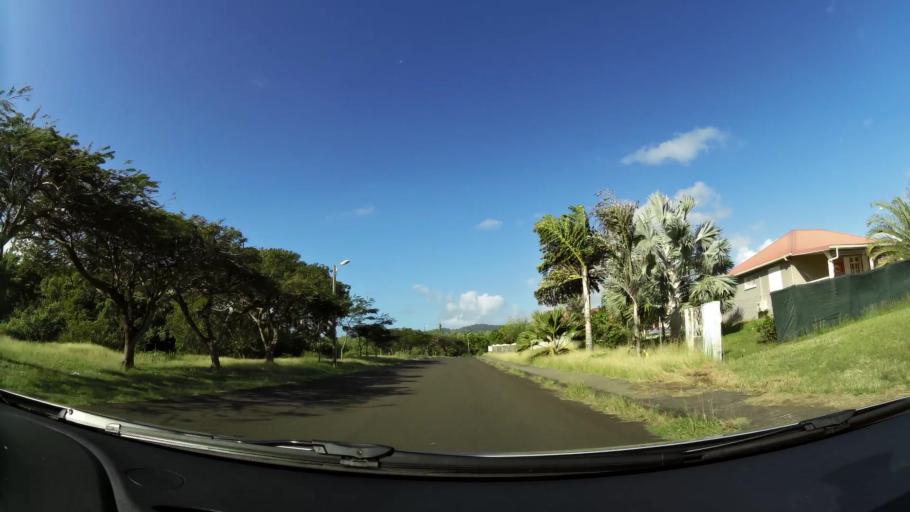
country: MQ
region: Martinique
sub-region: Martinique
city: Le Francois
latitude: 14.6200
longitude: -60.9004
